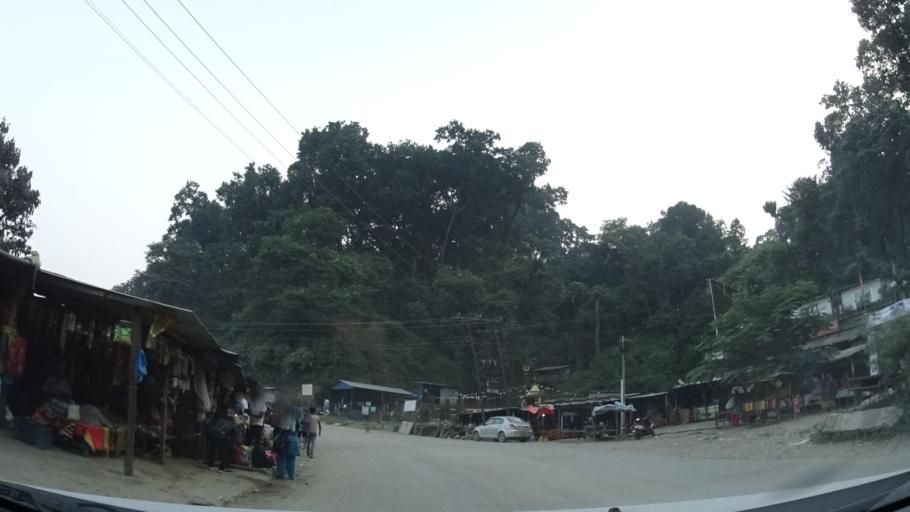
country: IN
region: Uttar Pradesh
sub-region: Maharajganj
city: Nichlaul
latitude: 27.5563
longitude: 83.8418
